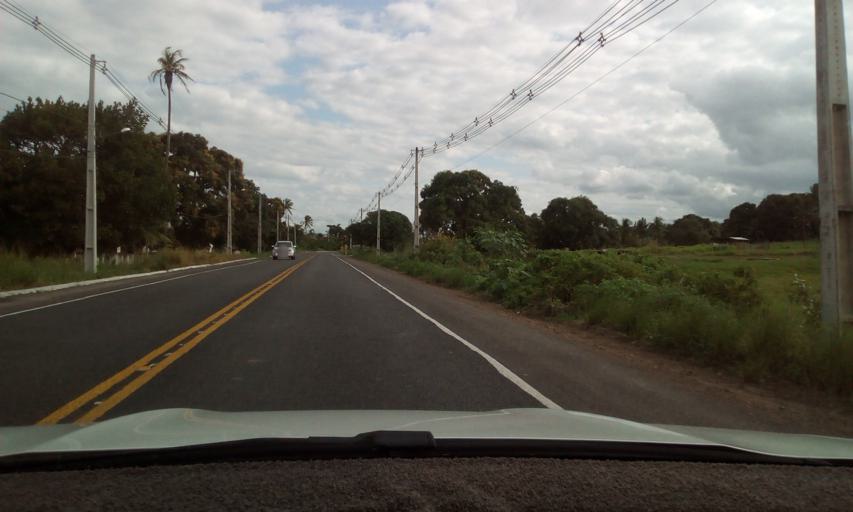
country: BR
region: Paraiba
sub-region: Mamanguape
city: Mamanguape
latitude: -6.8272
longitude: -35.1108
